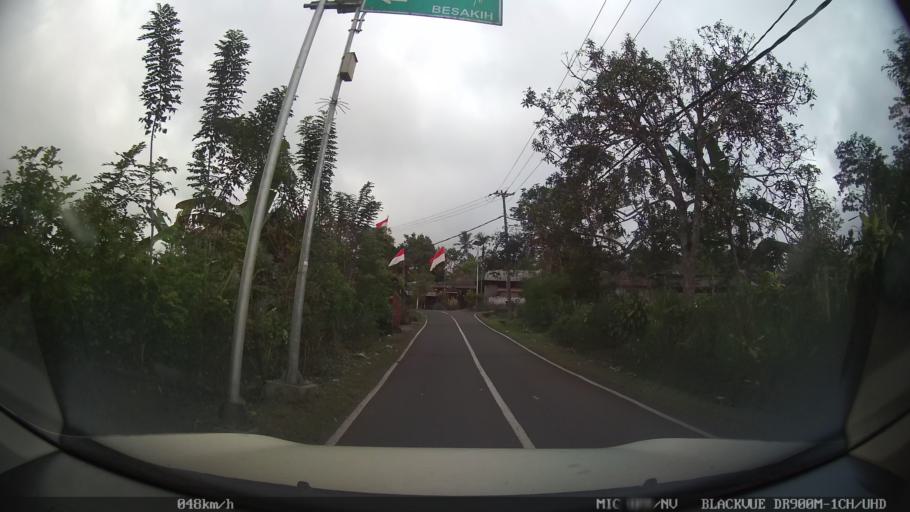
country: ID
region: Bali
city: Banjar Geriana Kangin
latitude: -8.3868
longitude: 115.4453
